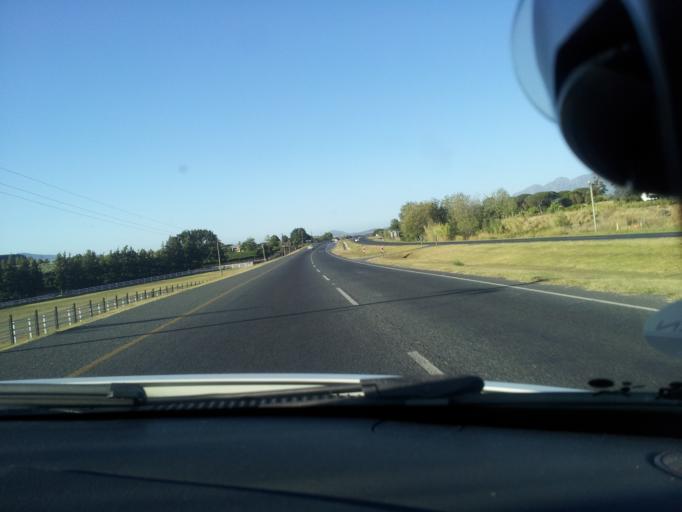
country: ZA
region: Western Cape
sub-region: Cape Winelands District Municipality
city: Stellenbosch
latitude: -34.0171
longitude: 18.8205
